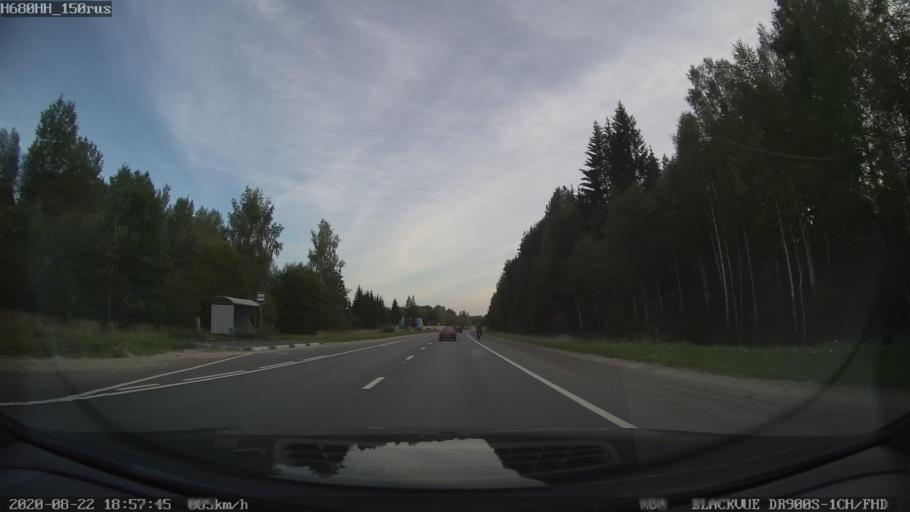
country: RU
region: Tverskaya
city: Rameshki
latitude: 57.1628
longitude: 36.0776
